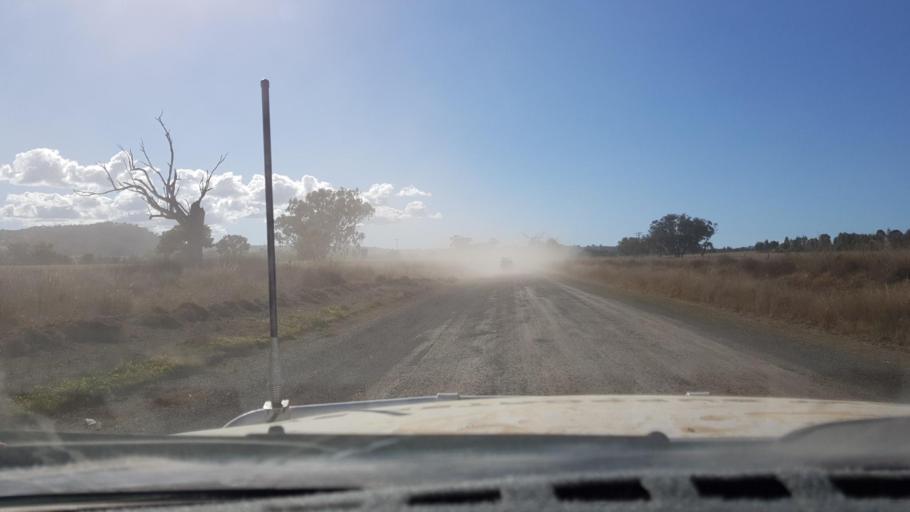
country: AU
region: New South Wales
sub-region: Narrabri
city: Blair Athol
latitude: -30.6728
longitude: 150.4505
